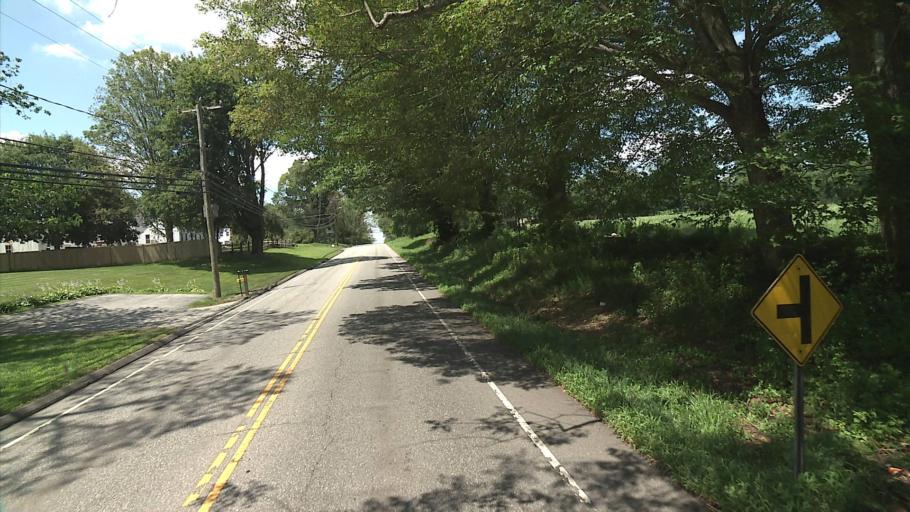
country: US
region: Connecticut
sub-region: Windham County
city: Windham
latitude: 41.7005
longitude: -72.1487
